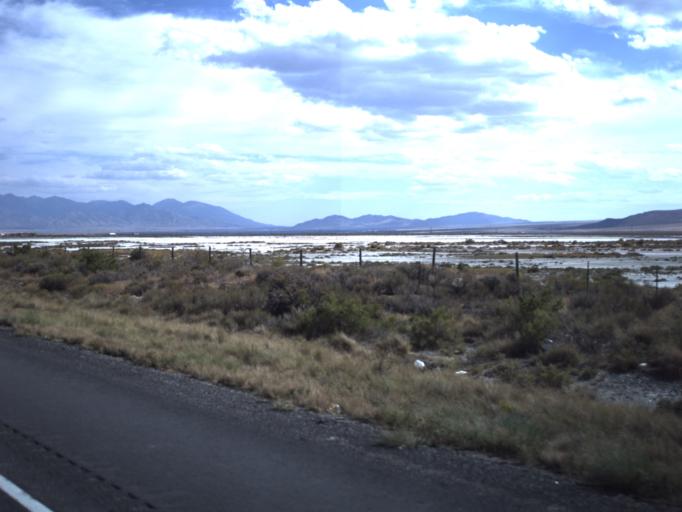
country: US
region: Utah
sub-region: Tooele County
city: Grantsville
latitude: 40.7153
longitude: -112.5441
